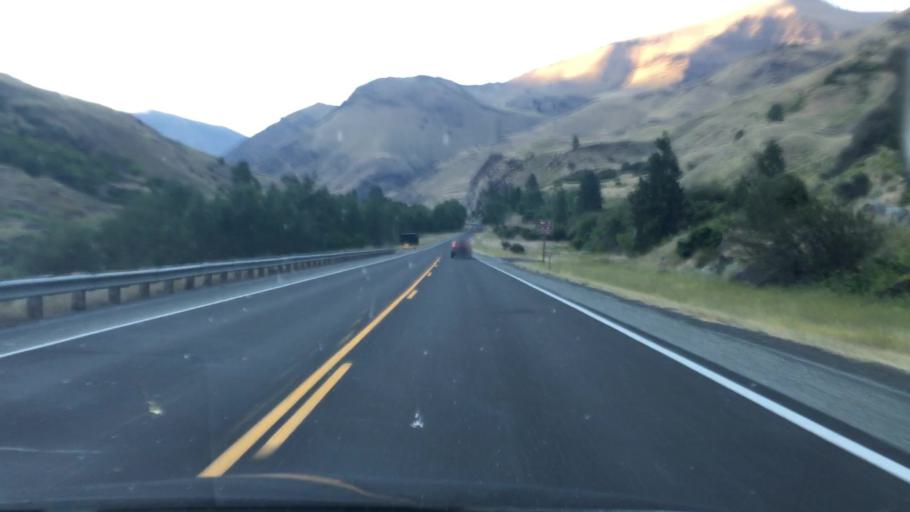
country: US
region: Idaho
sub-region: Valley County
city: McCall
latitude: 45.3224
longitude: -116.3485
